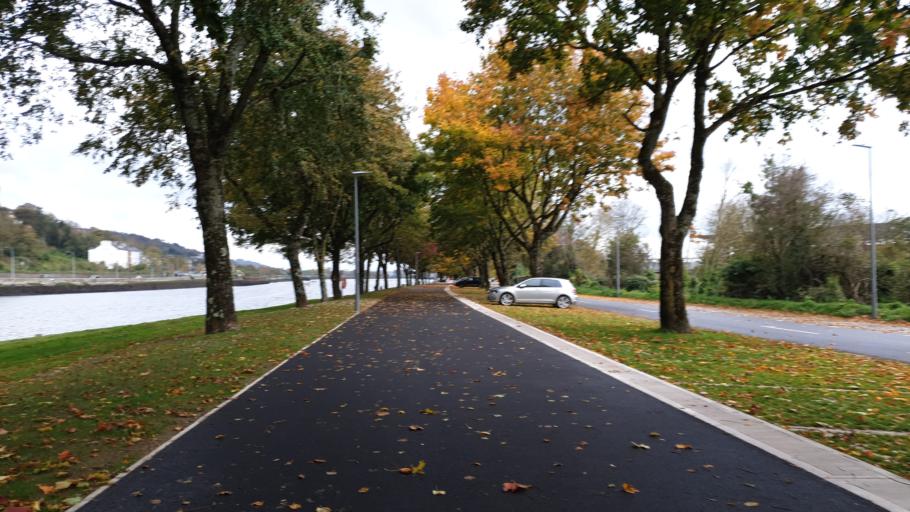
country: IE
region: Munster
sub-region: County Cork
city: Cork
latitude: 51.9015
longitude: -8.4408
